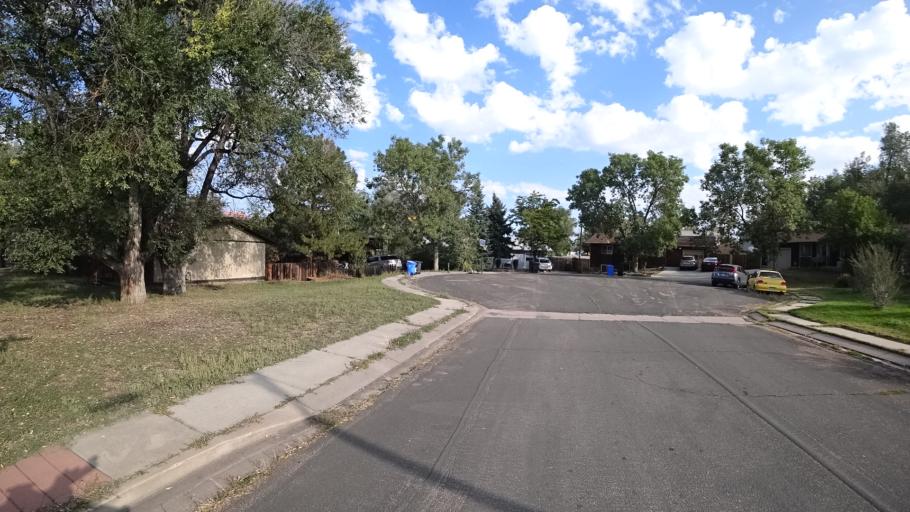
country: US
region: Colorado
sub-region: El Paso County
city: Colorado Springs
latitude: 38.8257
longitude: -104.8149
